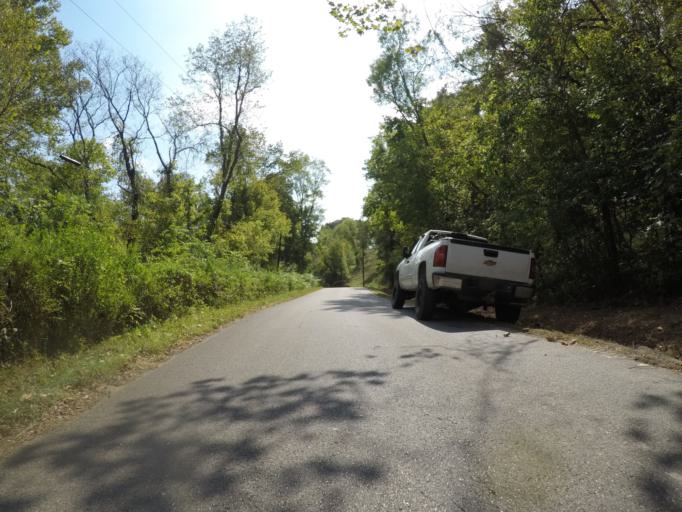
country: US
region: West Virginia
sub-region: Cabell County
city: Huntington
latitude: 38.4611
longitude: -82.4048
